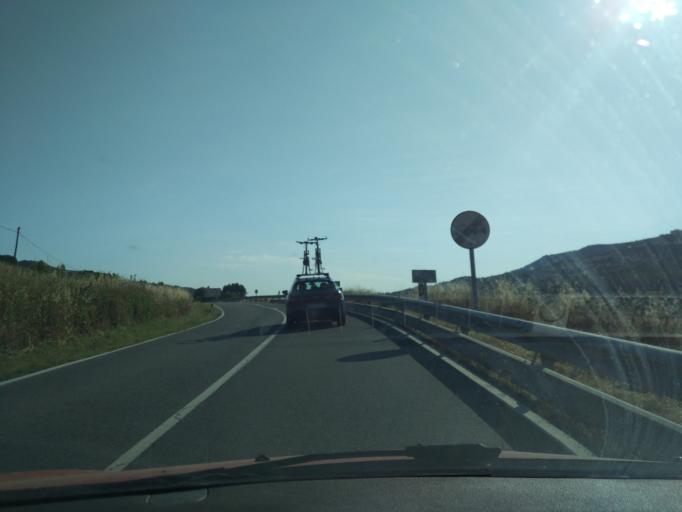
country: ES
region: Madrid
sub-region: Provincia de Madrid
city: Ambite
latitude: 40.3219
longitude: -3.1881
